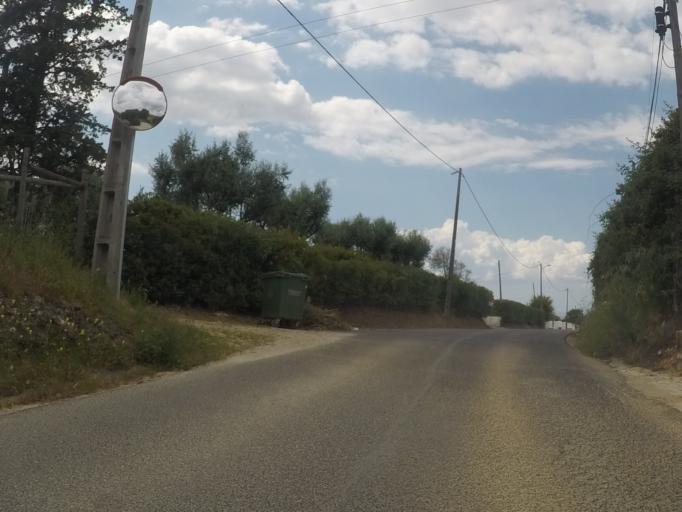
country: PT
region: Setubal
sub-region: Palmela
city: Quinta do Anjo
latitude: 38.5109
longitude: -9.0052
